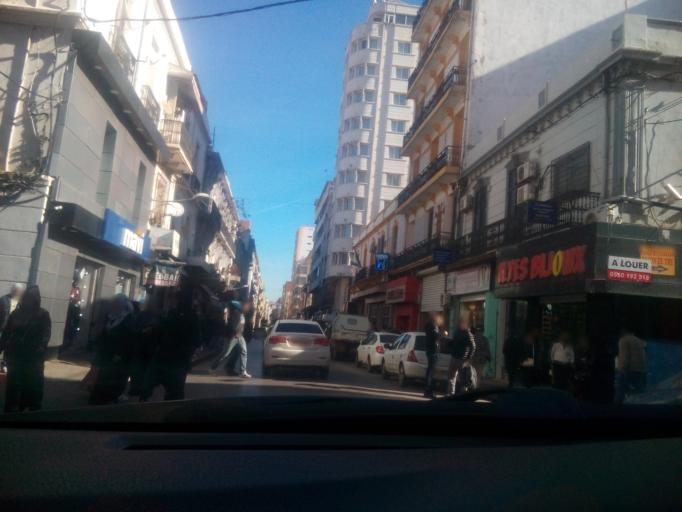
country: DZ
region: Oran
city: Oran
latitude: 35.7021
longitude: -0.6426
